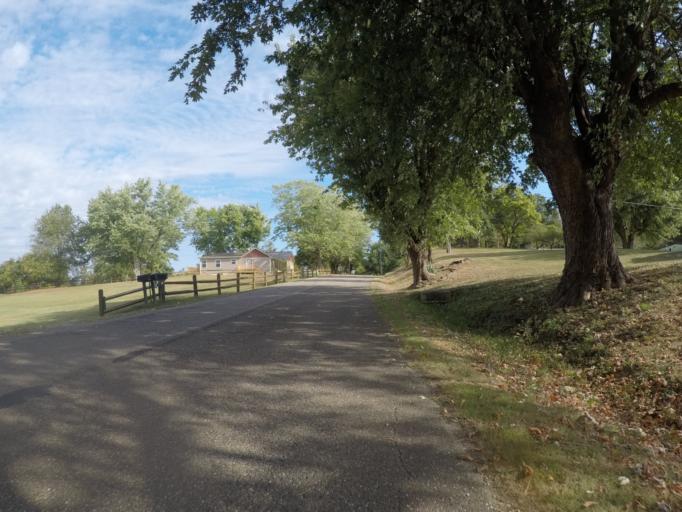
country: US
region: West Virginia
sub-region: Cabell County
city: Lesage
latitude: 38.5561
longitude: -82.4259
